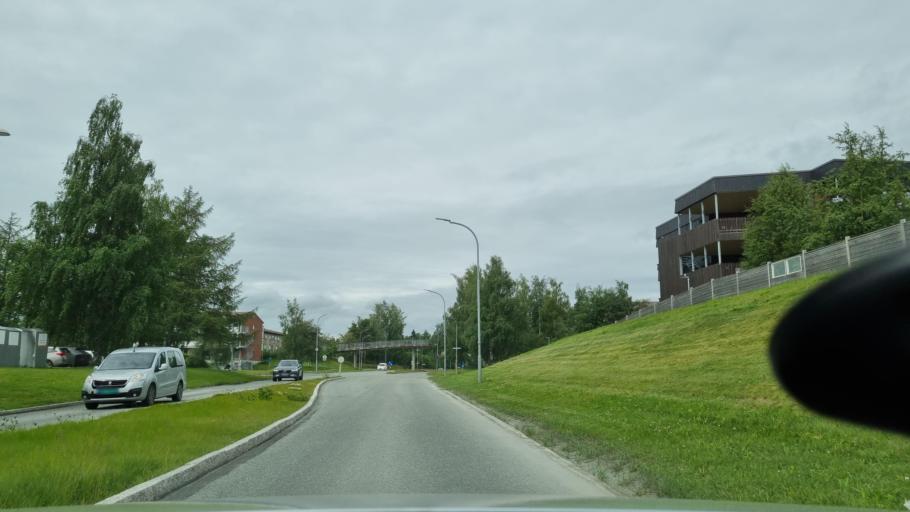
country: NO
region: Sor-Trondelag
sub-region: Melhus
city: Melhus
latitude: 63.3464
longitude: 10.3354
